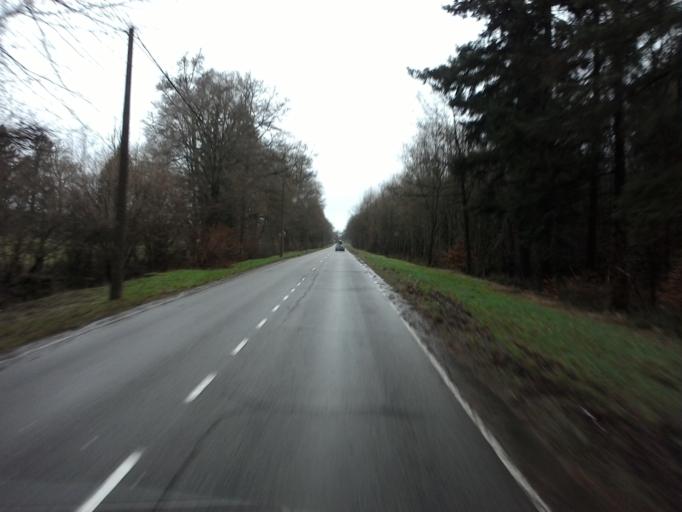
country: BE
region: Wallonia
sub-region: Province de Liege
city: Stavelot
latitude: 50.4147
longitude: 5.9309
